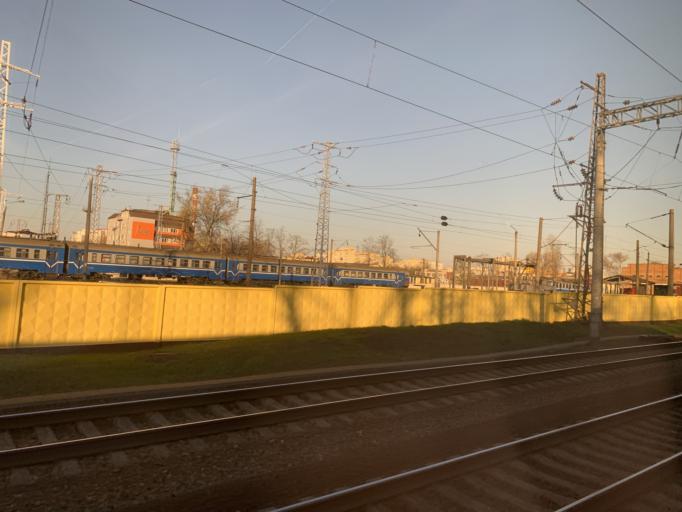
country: BY
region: Minsk
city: Minsk
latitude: 53.9176
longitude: 27.5166
